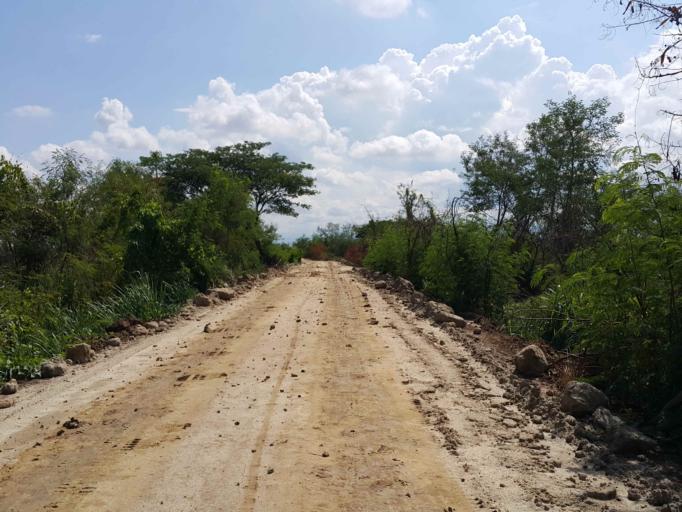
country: TH
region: Chiang Mai
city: San Kamphaeng
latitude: 18.7279
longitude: 99.0818
